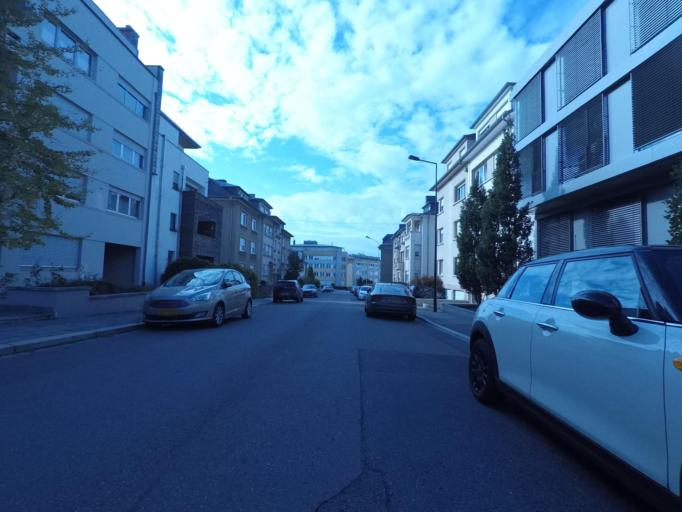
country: LU
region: Luxembourg
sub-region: Canton de Luxembourg
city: Luxembourg
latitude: 49.6054
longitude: 6.1151
